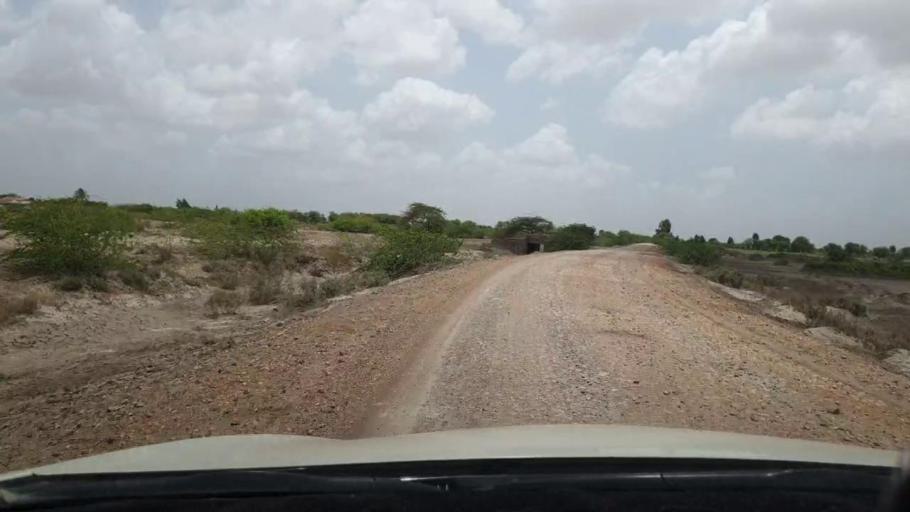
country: PK
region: Sindh
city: Kadhan
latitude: 24.3786
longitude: 68.9296
